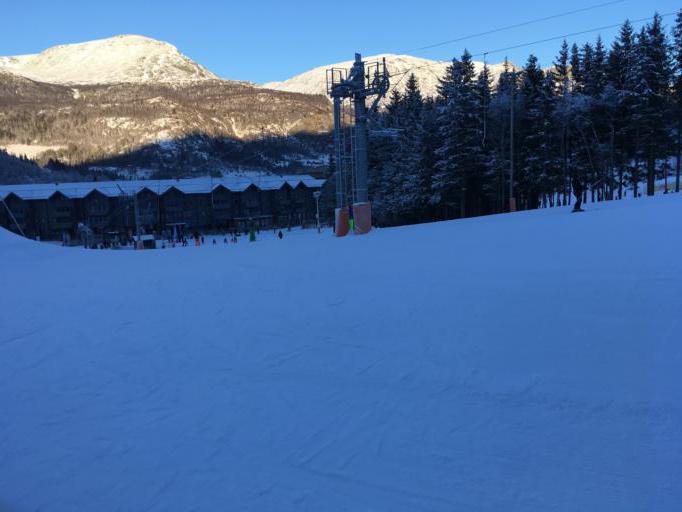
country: NO
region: Buskerud
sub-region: Hemsedal
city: Hemsedal
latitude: 60.8611
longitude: 8.5139
